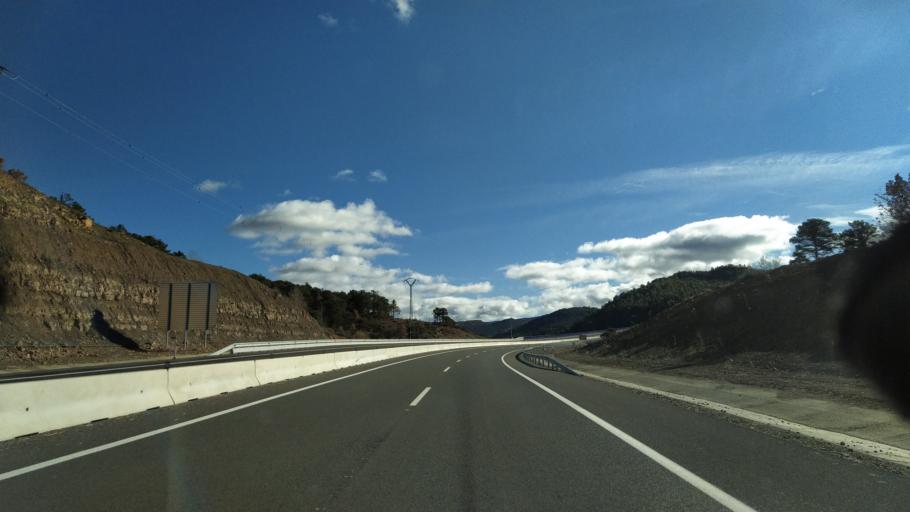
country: ES
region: Aragon
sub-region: Provincia de Huesca
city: Arguis
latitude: 42.4053
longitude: -0.3788
